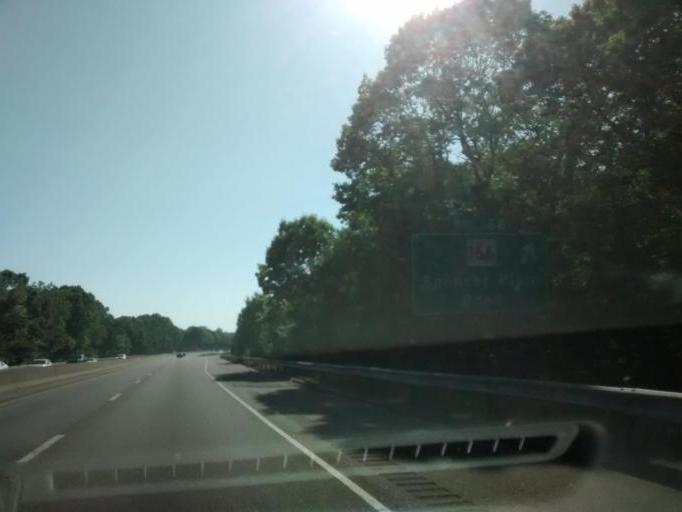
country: US
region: Connecticut
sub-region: Middlesex County
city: Saybrook Manor
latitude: 41.2923
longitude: -72.4127
